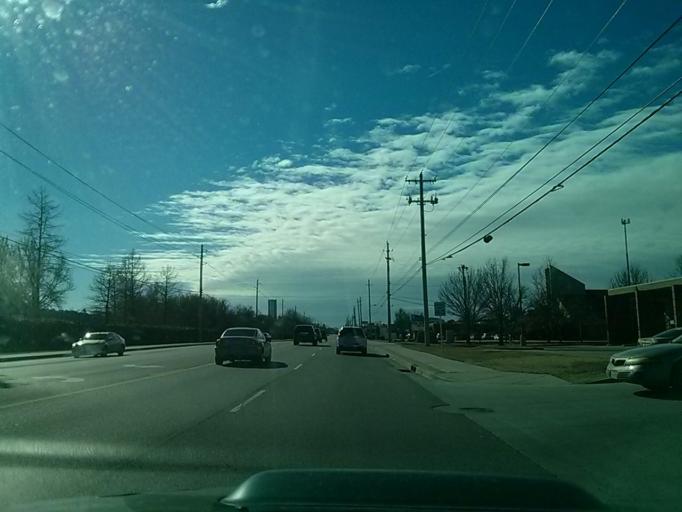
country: US
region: Oklahoma
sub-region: Tulsa County
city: Jenks
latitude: 36.0744
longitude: -95.9581
